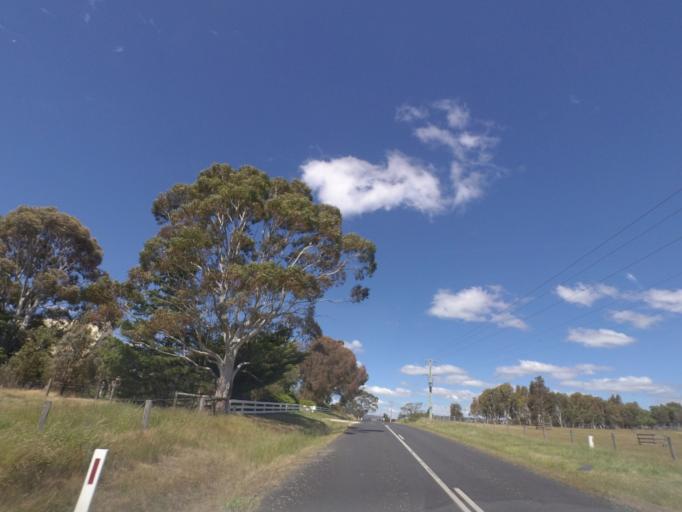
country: AU
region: Victoria
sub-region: Mount Alexander
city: Castlemaine
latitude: -37.2880
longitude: 144.4606
